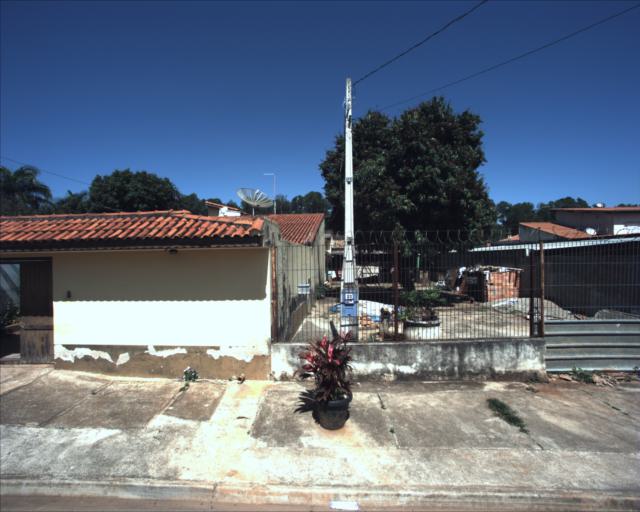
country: BR
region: Sao Paulo
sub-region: Aracoiaba Da Serra
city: Aracoiaba da Serra
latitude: -23.4409
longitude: -47.5376
